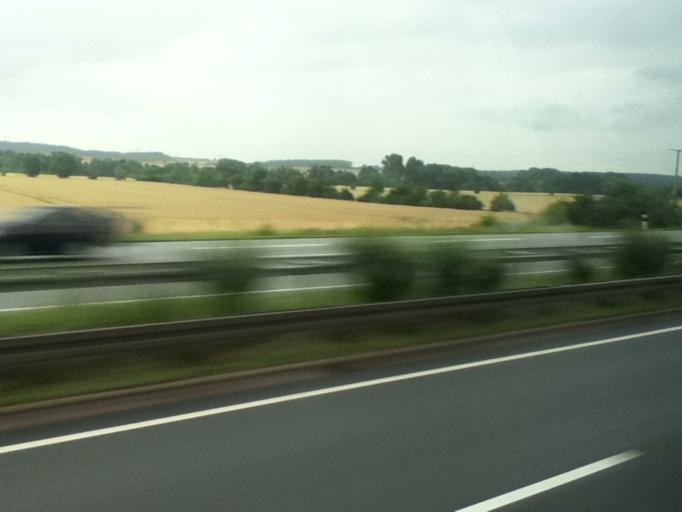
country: DE
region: Thuringia
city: Horselgau
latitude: 50.9094
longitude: 10.5914
